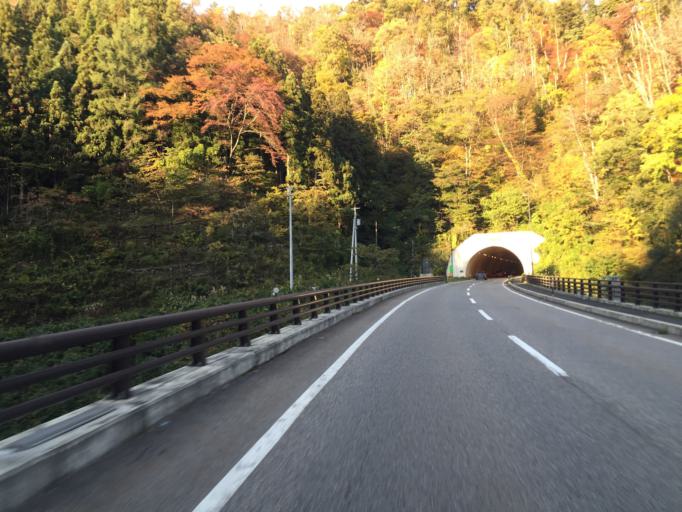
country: JP
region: Fukushima
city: Kitakata
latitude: 37.7460
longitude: 139.8874
